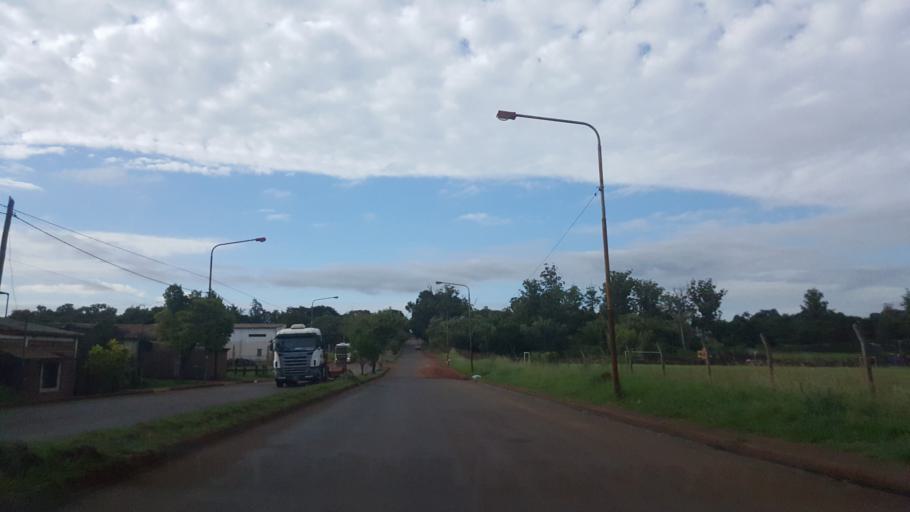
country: AR
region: Misiones
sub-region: Departamento de Capital
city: Posadas
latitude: -27.3939
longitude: -55.9354
